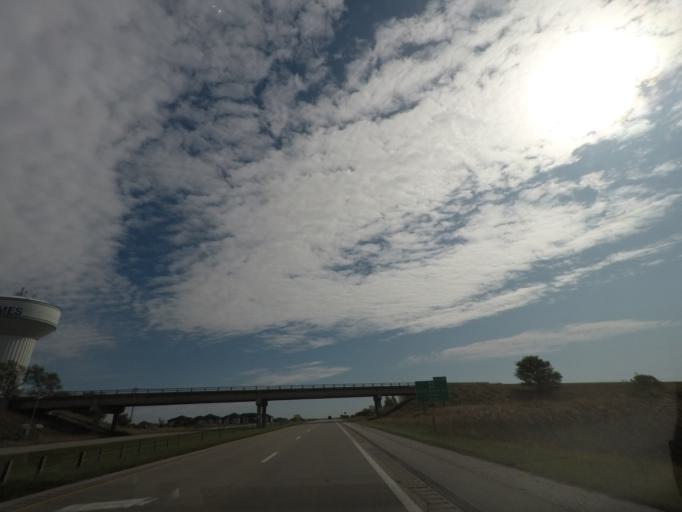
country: US
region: Iowa
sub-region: Story County
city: Ames
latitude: 42.0147
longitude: -93.6997
